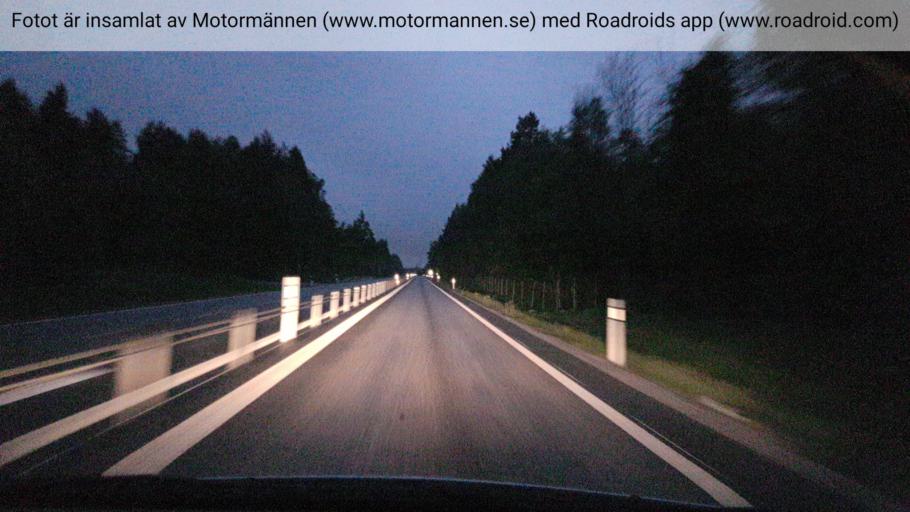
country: SE
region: Vaestmanland
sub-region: Surahammars Kommun
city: Surahammar
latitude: 59.7415
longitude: 16.2272
